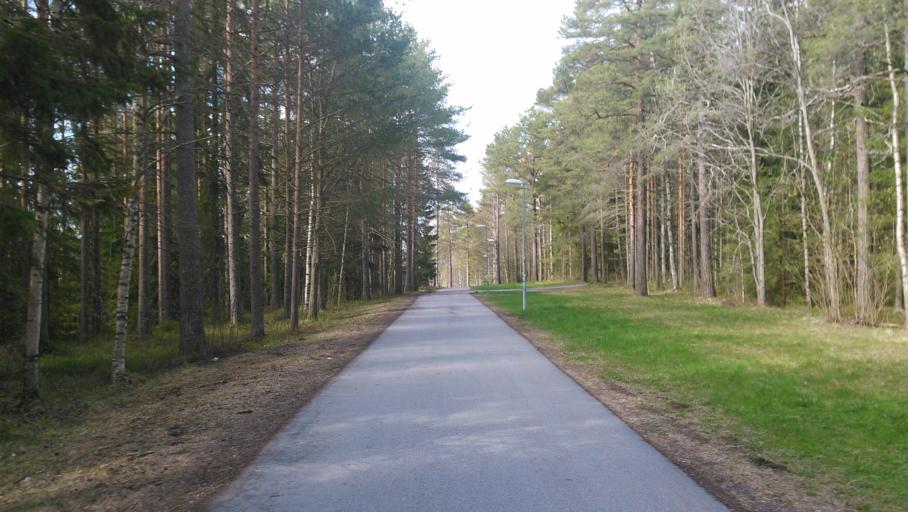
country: SE
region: Vaesterbotten
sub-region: Umea Kommun
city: Umea
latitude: 63.8052
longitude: 20.3169
